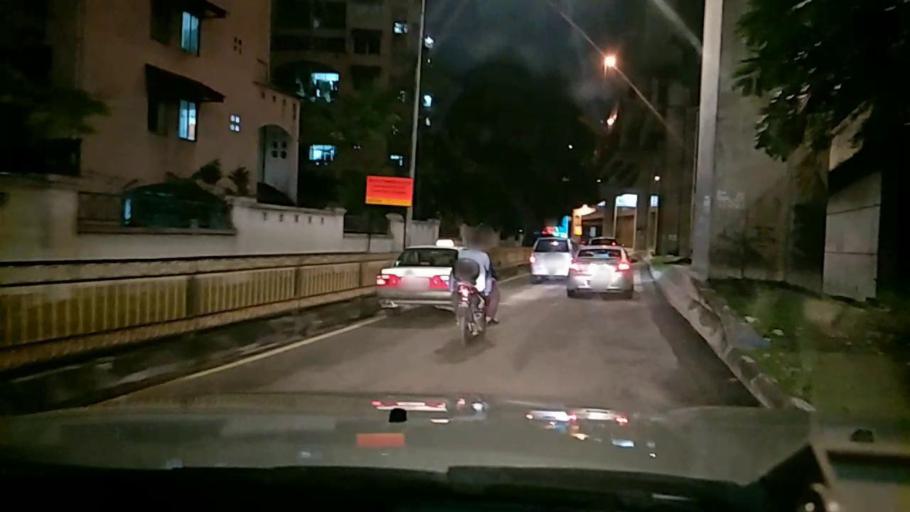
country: MY
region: Kuala Lumpur
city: Kuala Lumpur
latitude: 3.1367
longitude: 101.7188
